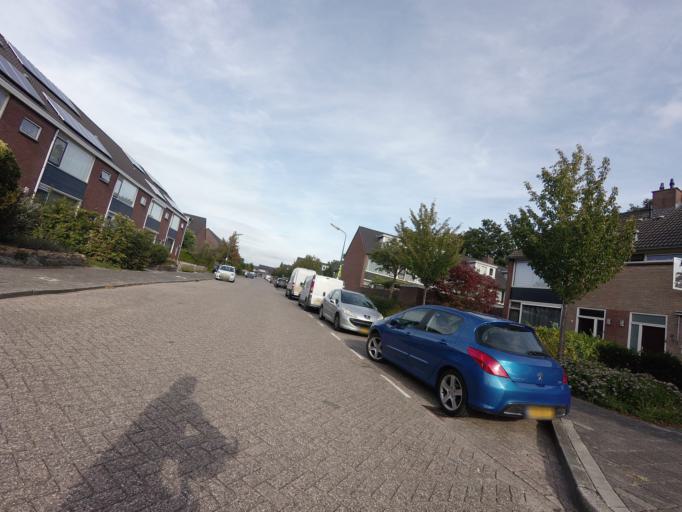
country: NL
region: Utrecht
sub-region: Gemeente Woerden
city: Woerden
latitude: 52.0882
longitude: 4.9005
